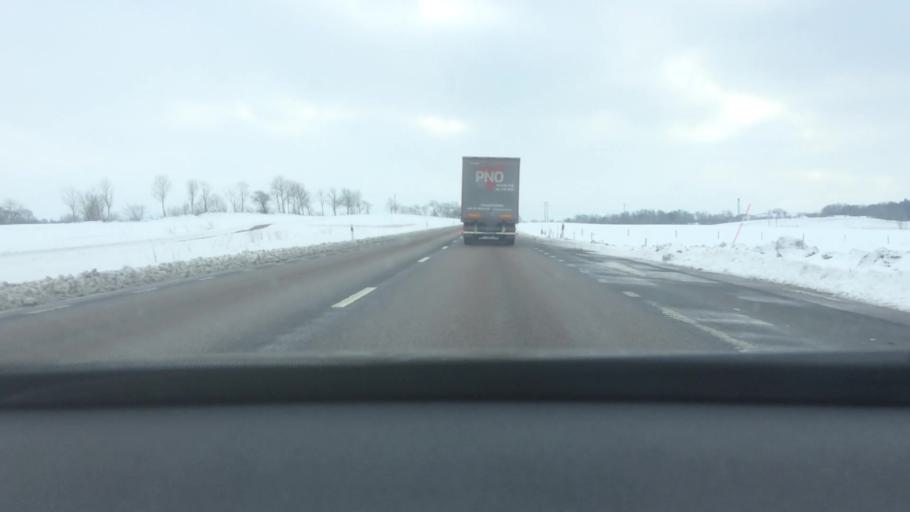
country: SE
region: Vaestra Goetaland
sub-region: Falkopings Kommun
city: Falkoeping
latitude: 58.2022
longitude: 13.5607
